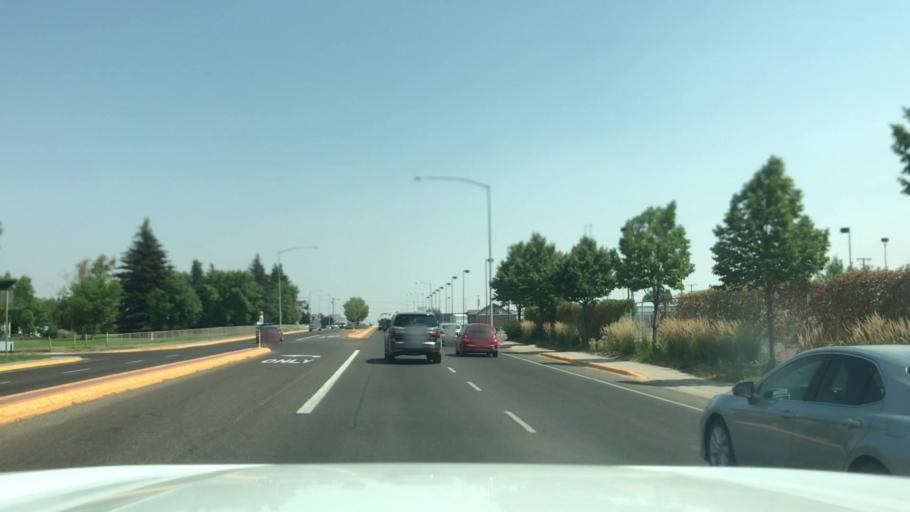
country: US
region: Montana
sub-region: Cascade County
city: Great Falls
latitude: 47.4941
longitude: -111.2616
